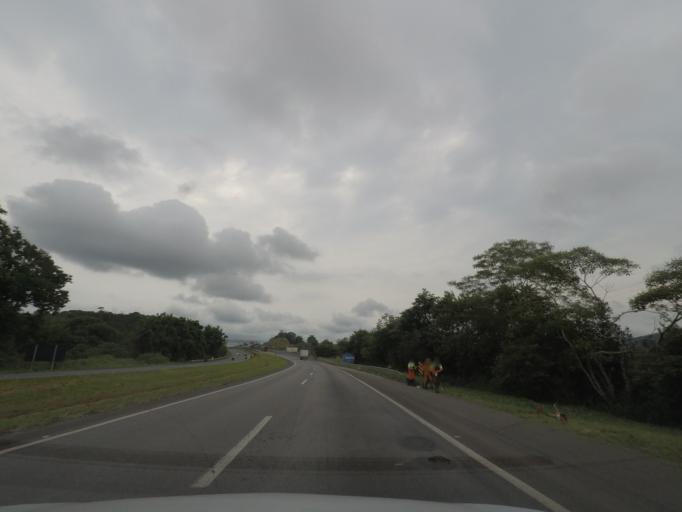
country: BR
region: Sao Paulo
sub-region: Juquia
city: Juquia
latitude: -24.3297
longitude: -47.6179
